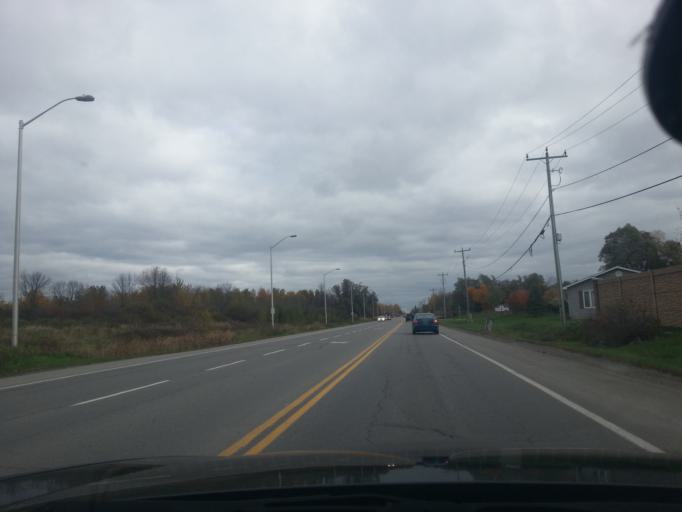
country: CA
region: Ontario
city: Ottawa
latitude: 45.2670
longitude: -75.5996
